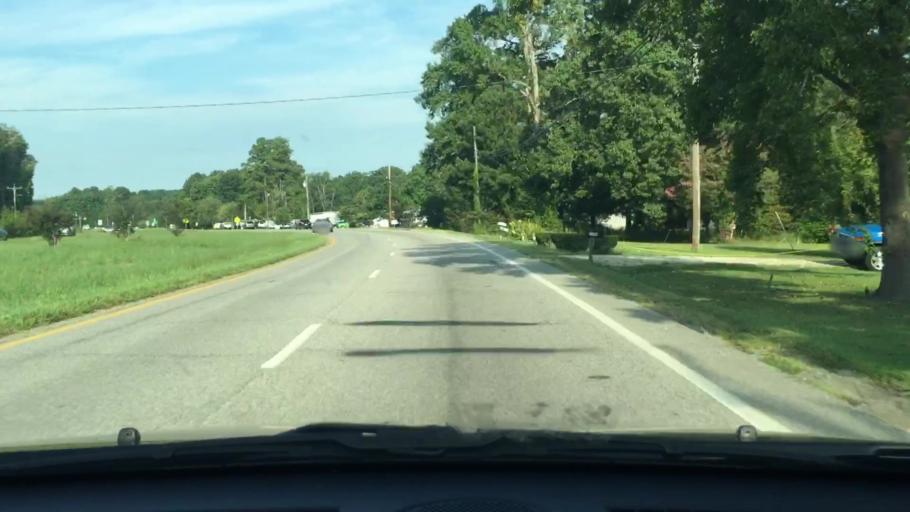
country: US
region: Virginia
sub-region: Isle of Wight County
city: Carrollton
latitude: 36.9432
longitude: -76.5506
